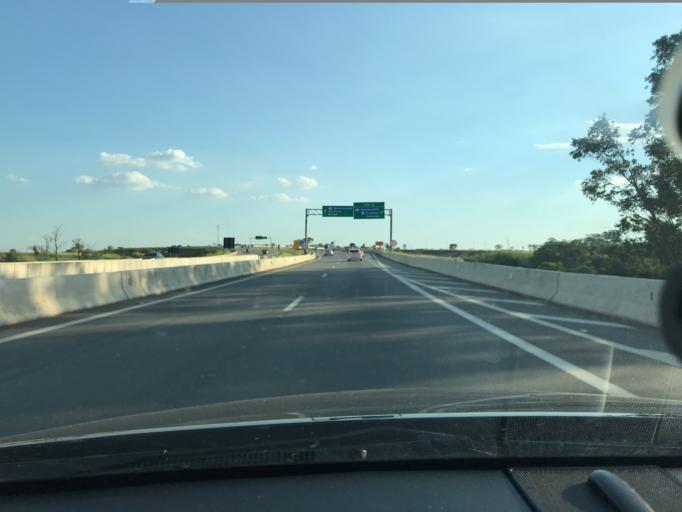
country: BR
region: Sao Paulo
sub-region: Valinhos
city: Valinhos
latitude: -23.0093
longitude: -47.0845
